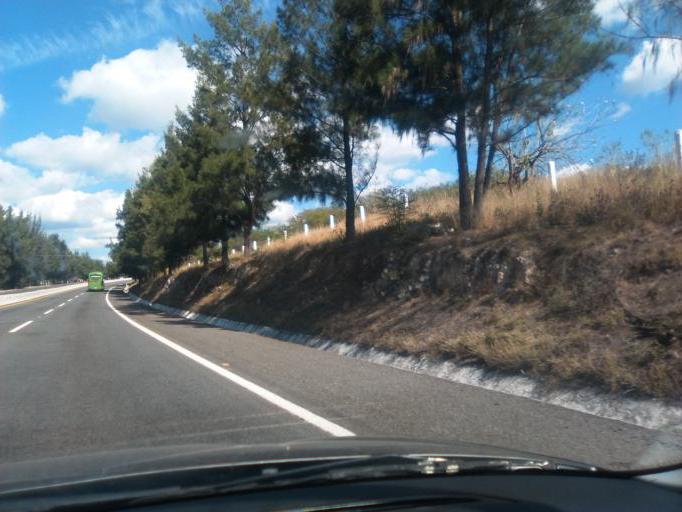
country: MX
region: Guanajuato
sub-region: Guanajuato
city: San Jose de Cervera
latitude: 20.9740
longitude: -101.3027
